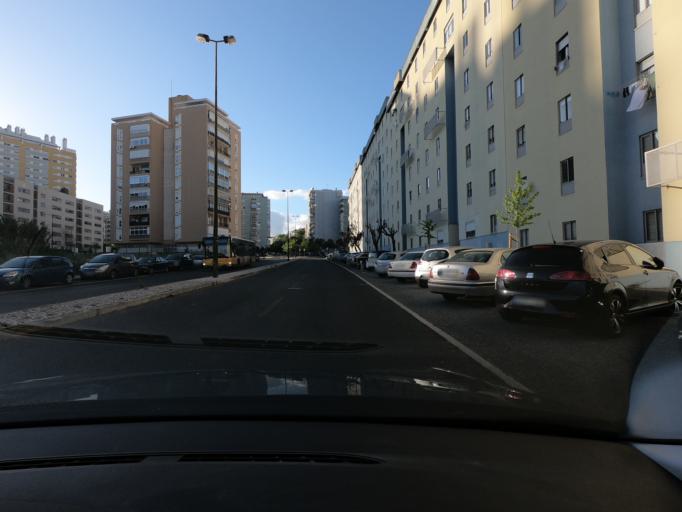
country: PT
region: Lisbon
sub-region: Lisbon
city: Lisbon
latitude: 38.7269
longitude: -9.1232
